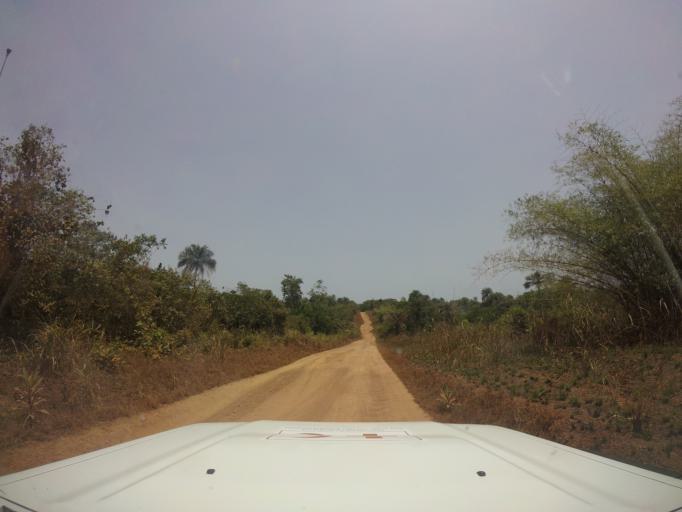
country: LR
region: Grand Cape Mount
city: Robertsport
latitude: 6.9439
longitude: -11.3262
